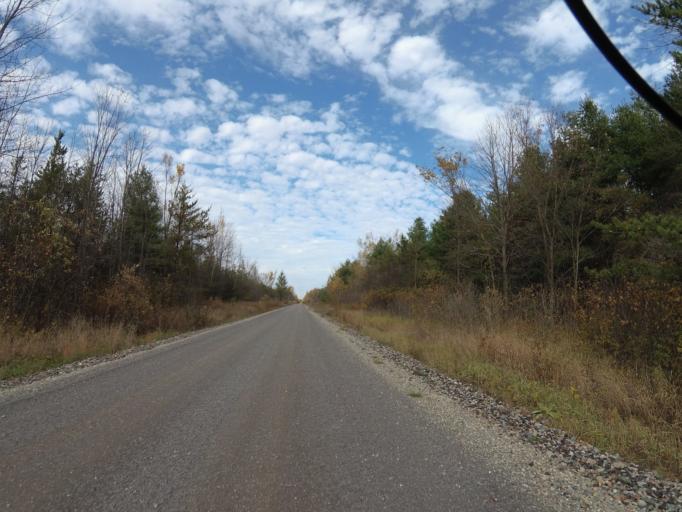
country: CA
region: Ontario
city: Carleton Place
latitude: 45.0734
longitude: -76.1004
